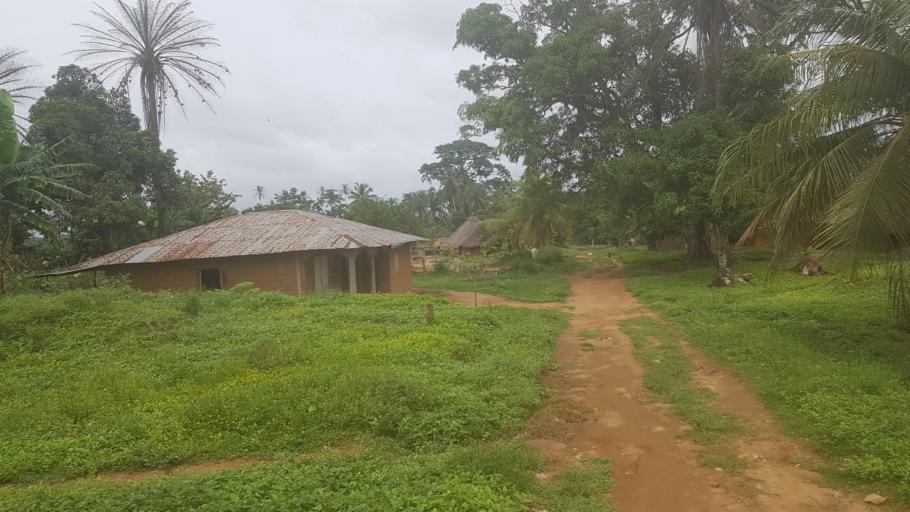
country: SL
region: Southern Province
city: Sumbuya
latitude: 7.5334
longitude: -12.1775
